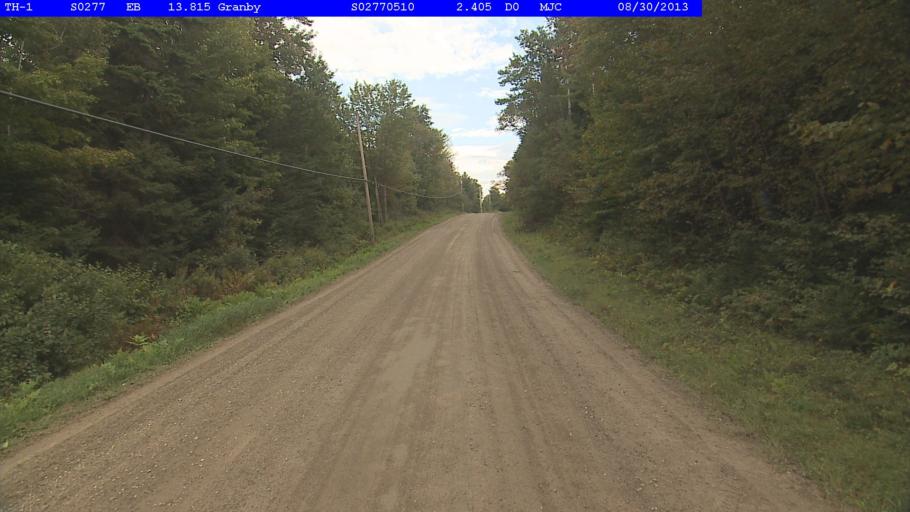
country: US
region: Vermont
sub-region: Essex County
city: Guildhall
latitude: 44.5779
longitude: -71.7189
